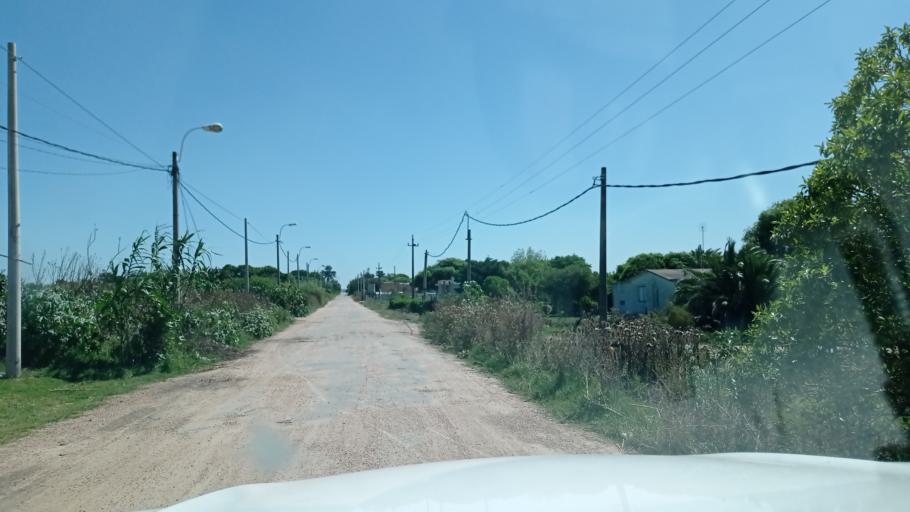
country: UY
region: Montevideo
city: Pajas Blancas
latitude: -34.8692
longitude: -56.2733
